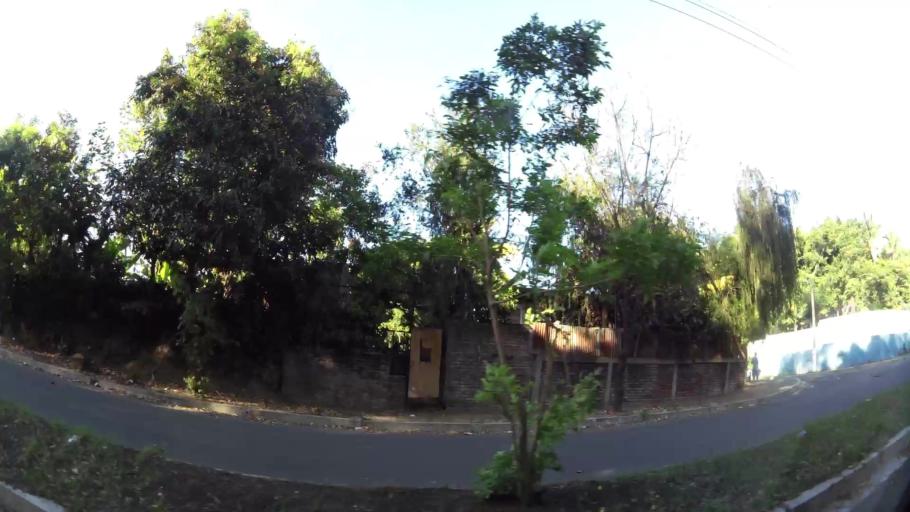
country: SV
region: La Libertad
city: Santa Tecla
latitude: 13.7350
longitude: -89.3541
